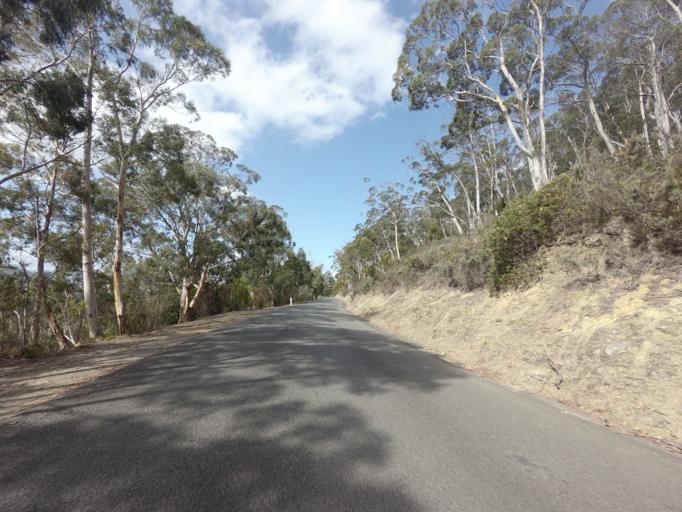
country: AU
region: Tasmania
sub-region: Hobart
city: Dynnyrne
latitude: -42.9159
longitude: 147.2785
